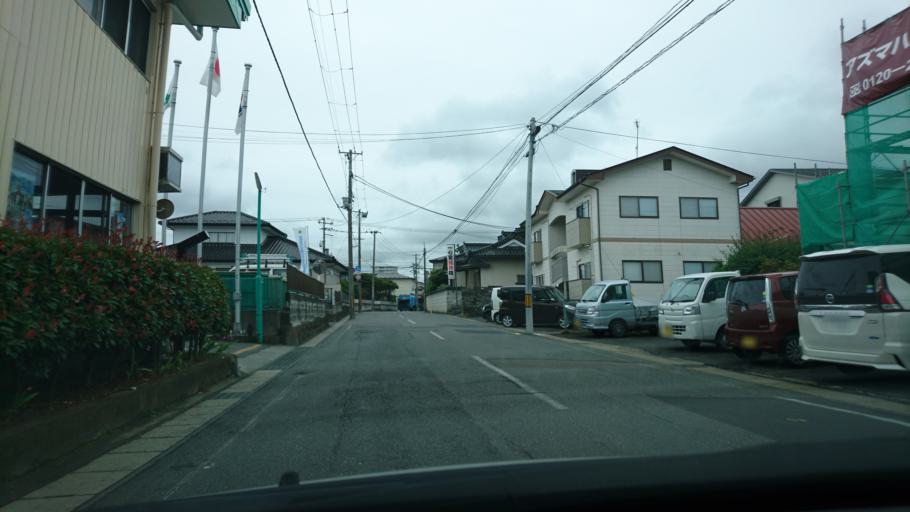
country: JP
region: Iwate
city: Ichinoseki
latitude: 38.9338
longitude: 141.1384
